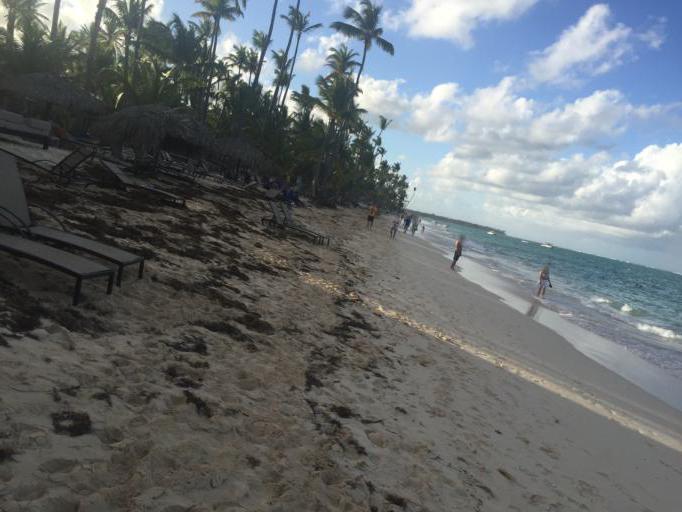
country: DO
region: San Juan
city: Punta Cana
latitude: 18.6932
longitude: -68.4240
